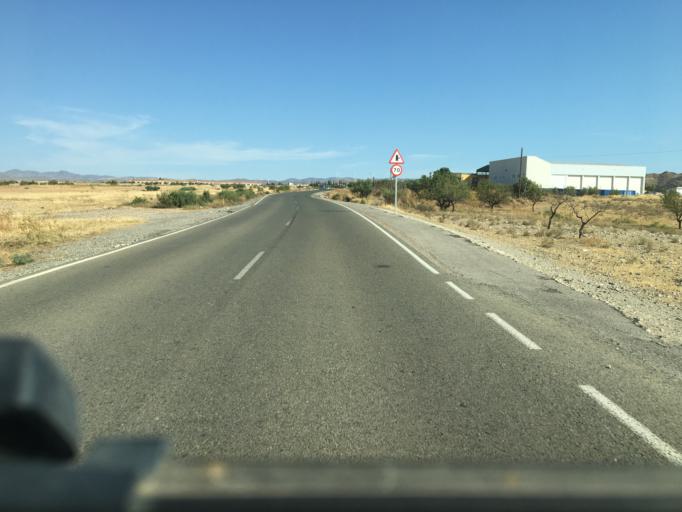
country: ES
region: Andalusia
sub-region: Provincia de Almeria
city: Huercal-Overa
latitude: 37.4381
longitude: -1.9761
